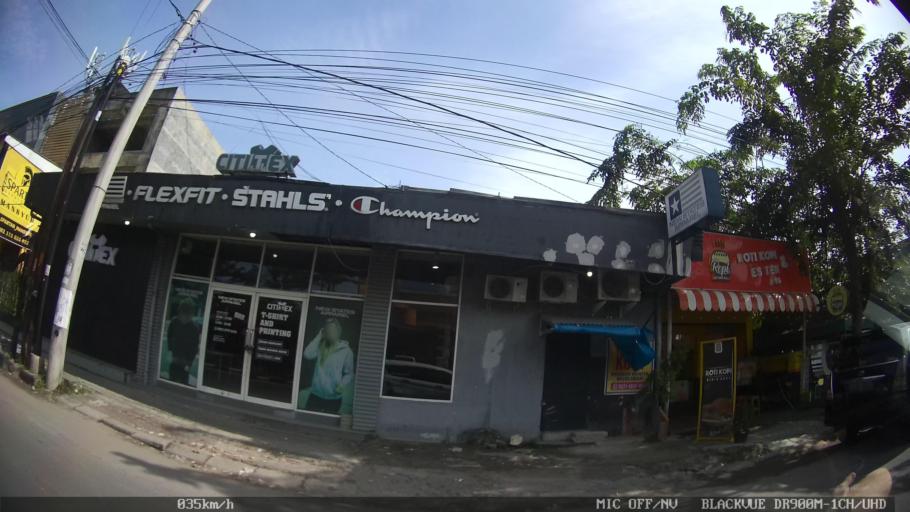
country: ID
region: North Sumatra
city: Medan
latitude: 3.5676
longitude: 98.6470
